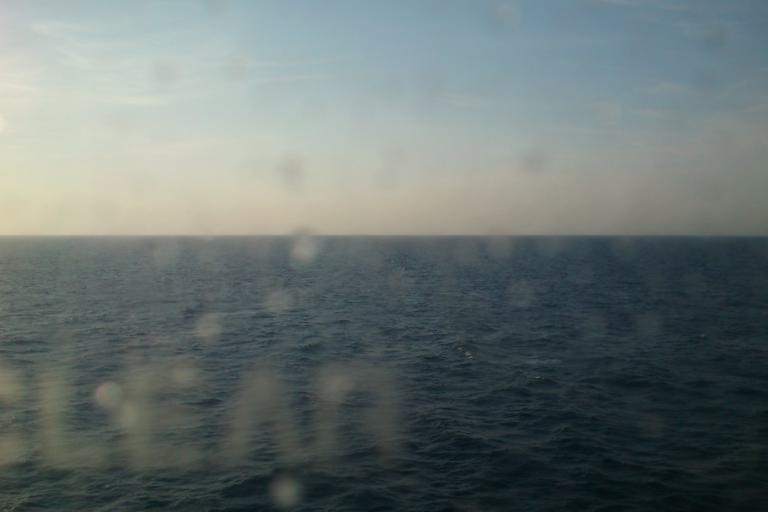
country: JP
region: Ishikawa
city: Nanao
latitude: 37.7743
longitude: 136.4226
